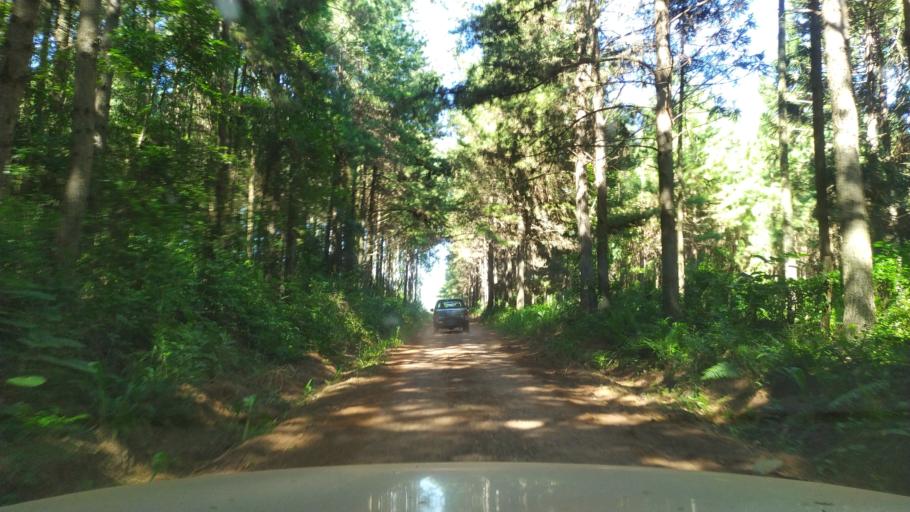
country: AR
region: Misiones
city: Caraguatay
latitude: -26.6771
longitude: -54.7024
